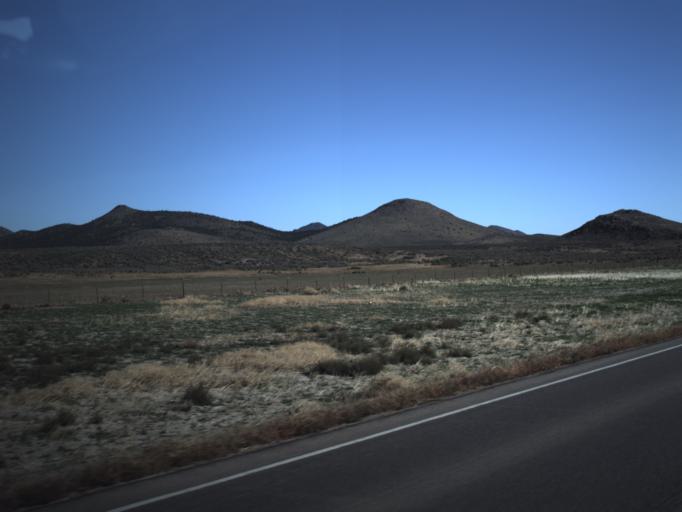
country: US
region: Utah
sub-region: Washington County
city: Enterprise
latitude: 37.7864
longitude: -113.9579
